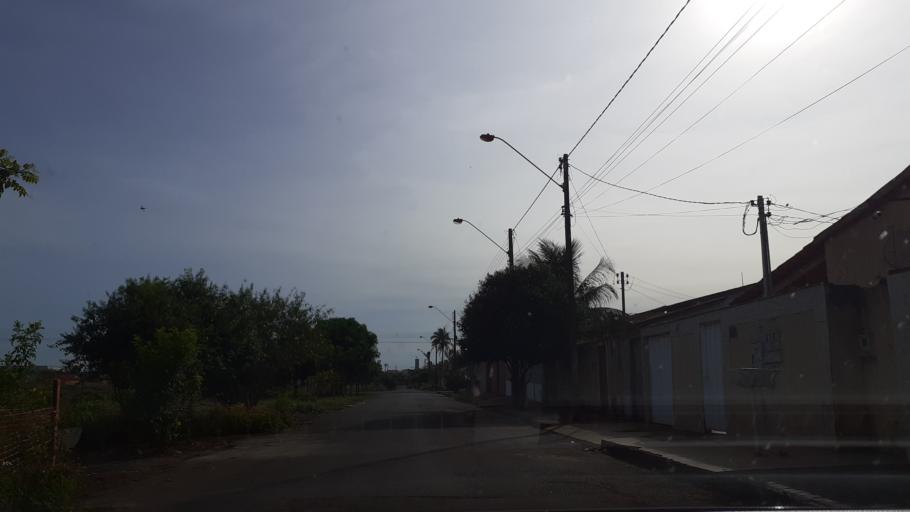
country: BR
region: Goias
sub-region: Itumbiara
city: Itumbiara
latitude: -18.4172
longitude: -49.2470
